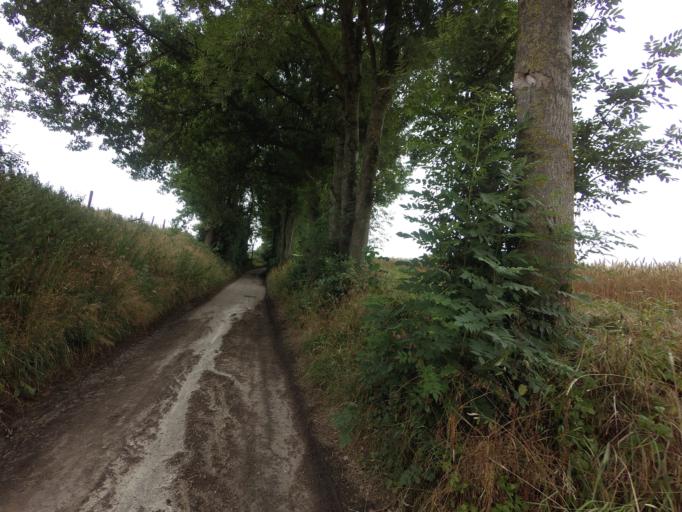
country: NL
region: Limburg
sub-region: Eijsden-Margraten
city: Margraten
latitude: 50.8140
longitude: 5.8181
